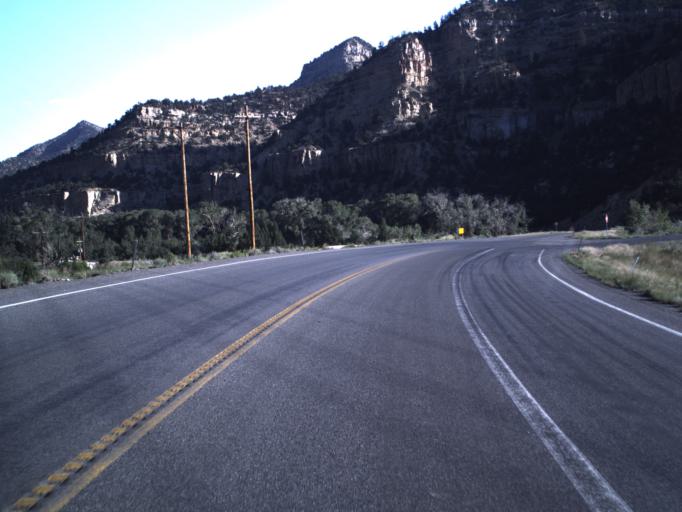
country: US
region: Utah
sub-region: Emery County
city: Huntington
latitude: 39.3978
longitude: -111.1099
